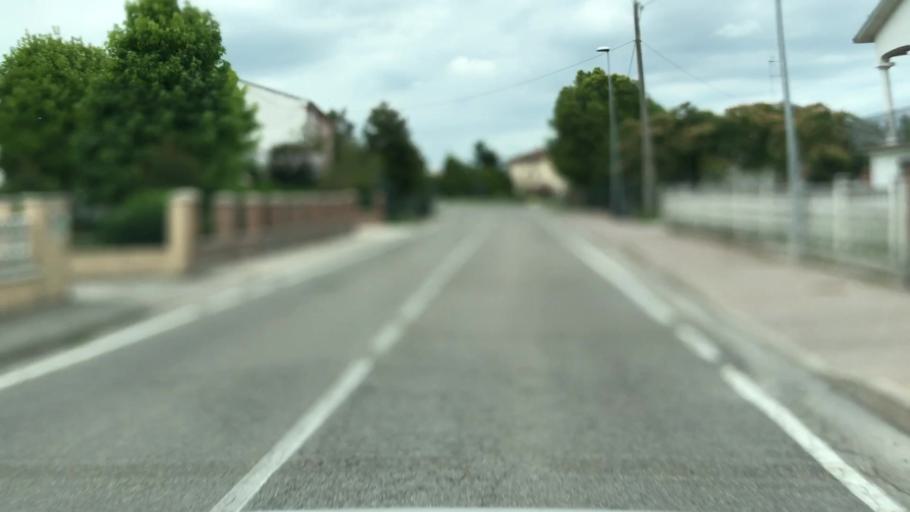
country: IT
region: Lombardy
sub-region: Provincia di Mantova
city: Quistello
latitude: 45.0321
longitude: 11.0059
